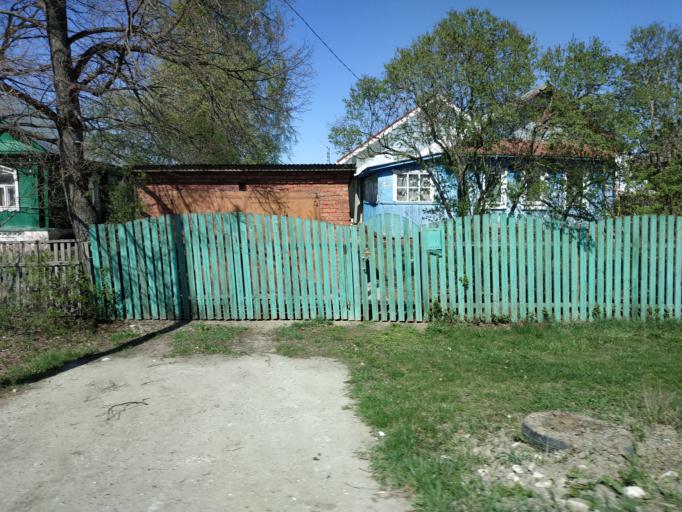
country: RU
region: Moskovskaya
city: Malyshevo
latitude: 55.4624
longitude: 38.3469
